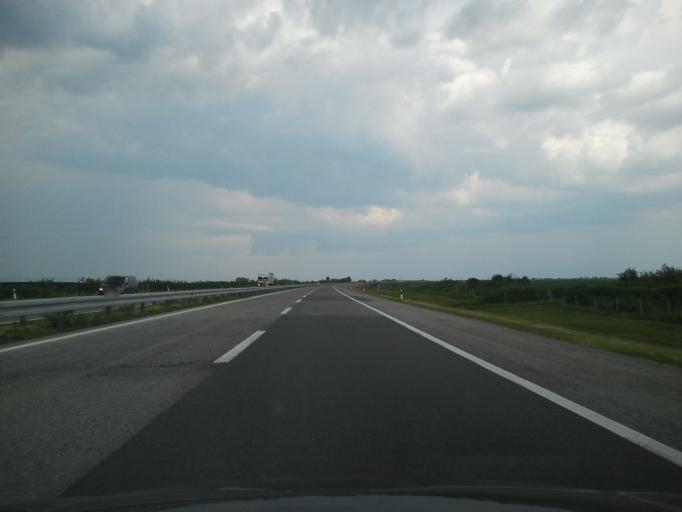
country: RS
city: Visnjicevo
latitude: 45.0411
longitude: 19.3413
